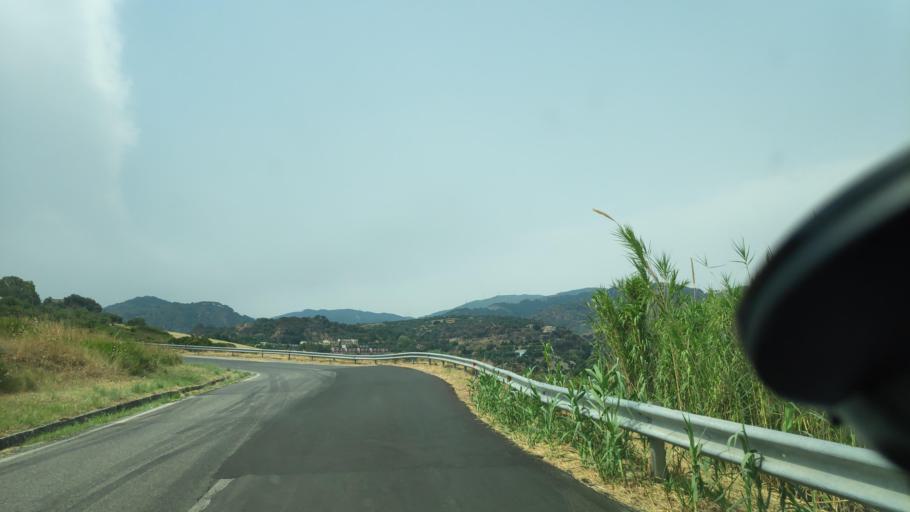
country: IT
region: Calabria
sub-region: Provincia di Catanzaro
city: Marina di Davoli
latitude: 38.6498
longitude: 16.5408
